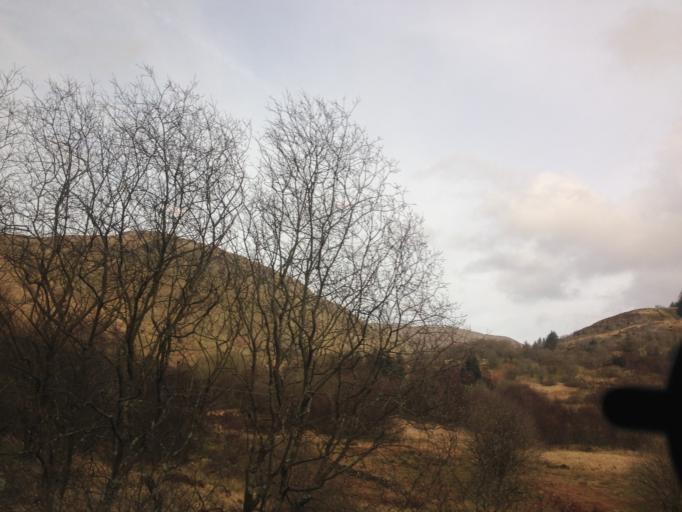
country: GB
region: Scotland
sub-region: Argyll and Bute
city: Garelochhead
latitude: 56.1535
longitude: -4.7805
